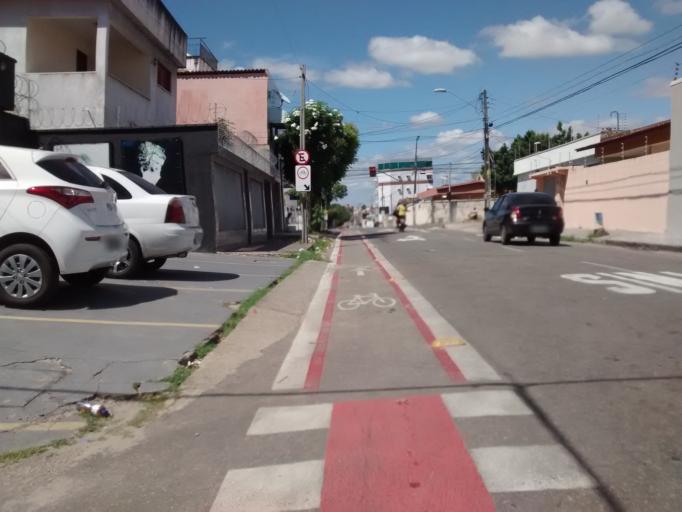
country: BR
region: Ceara
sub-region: Fortaleza
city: Fortaleza
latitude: -3.7395
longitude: -38.5576
